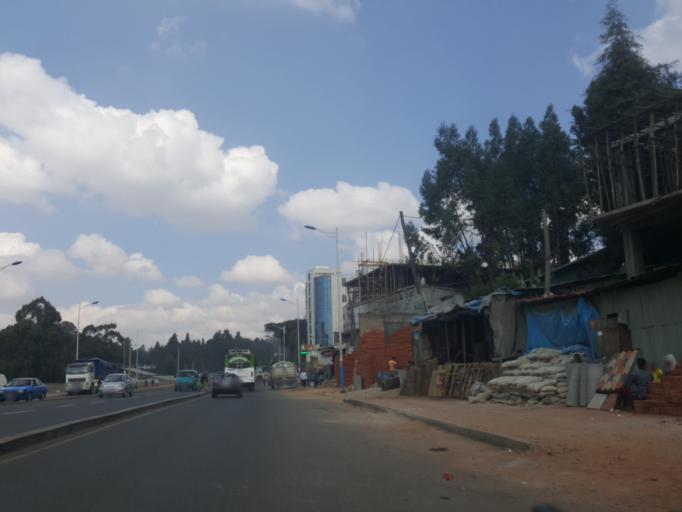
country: ET
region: Adis Abeba
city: Addis Ababa
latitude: 9.0536
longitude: 38.7193
